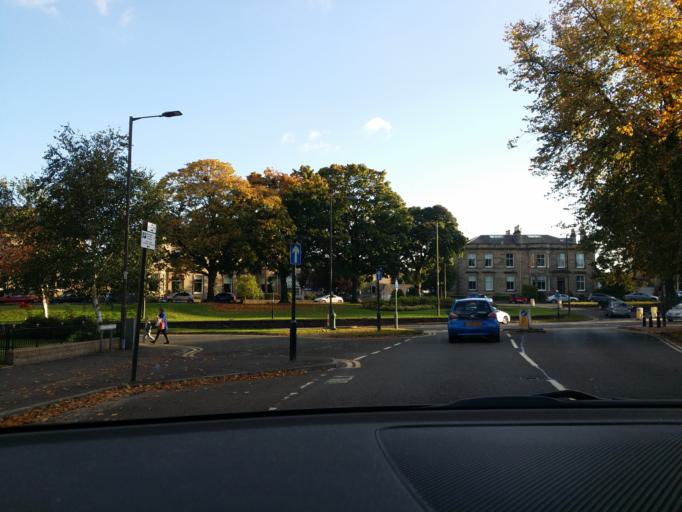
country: GB
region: Scotland
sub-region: Stirling
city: Stirling
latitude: 56.1140
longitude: -3.9452
